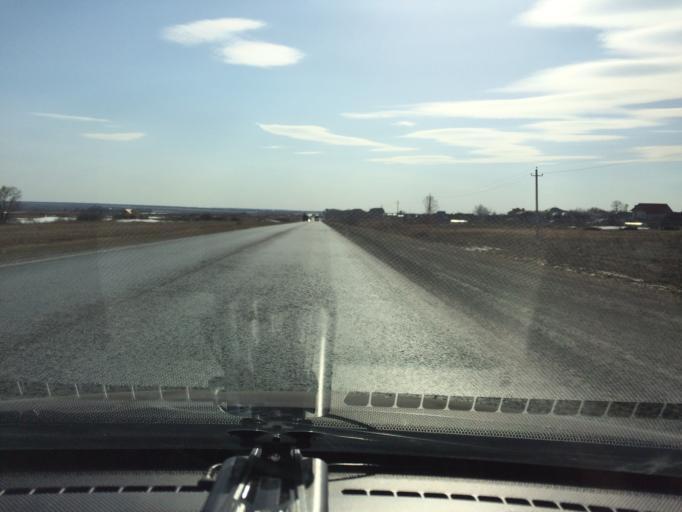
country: RU
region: Mariy-El
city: Yoshkar-Ola
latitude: 56.7146
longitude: 48.0924
